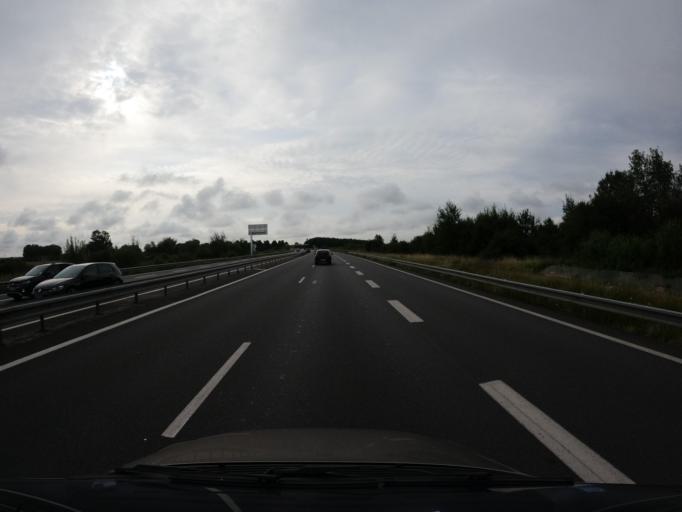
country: FR
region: Centre
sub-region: Departement d'Indre-et-Loire
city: Villandry
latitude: 47.3093
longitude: 0.5125
